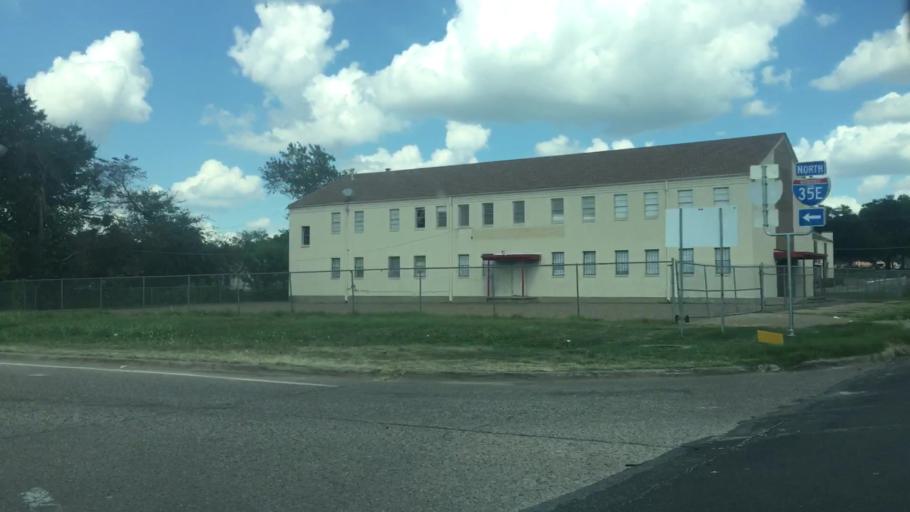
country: US
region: Texas
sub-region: Dallas County
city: Cockrell Hill
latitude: 32.7132
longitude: -96.8283
